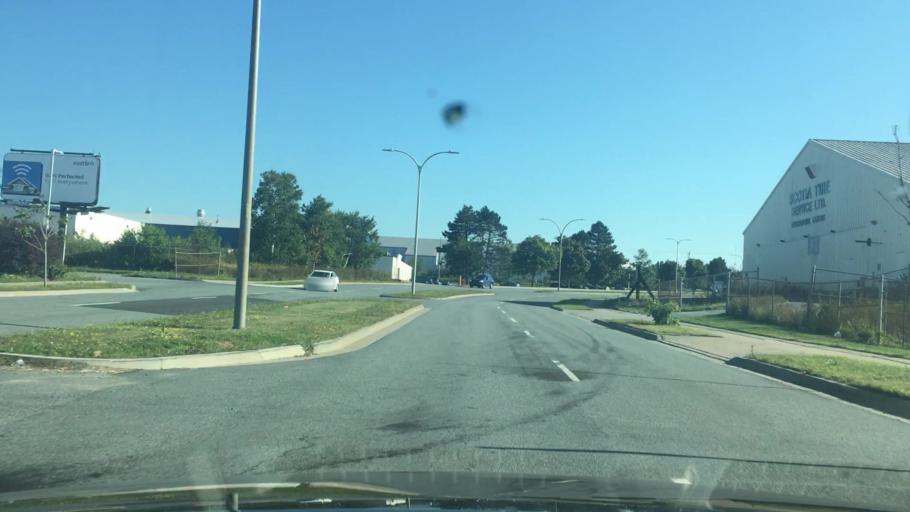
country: CA
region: Nova Scotia
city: Dartmouth
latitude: 44.7091
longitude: -63.6061
